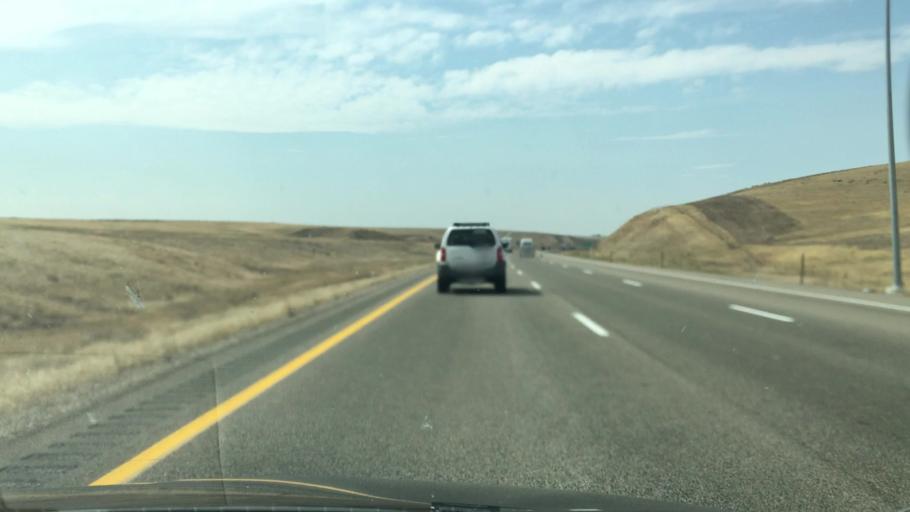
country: US
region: Idaho
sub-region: Ada County
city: Boise
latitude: 43.4859
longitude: -116.1177
